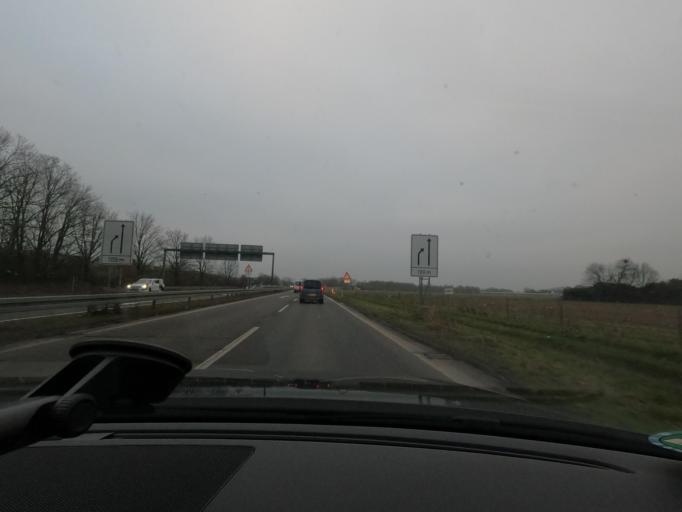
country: DE
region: North Rhine-Westphalia
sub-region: Regierungsbezirk Dusseldorf
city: Willich
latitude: 51.2922
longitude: 6.5261
